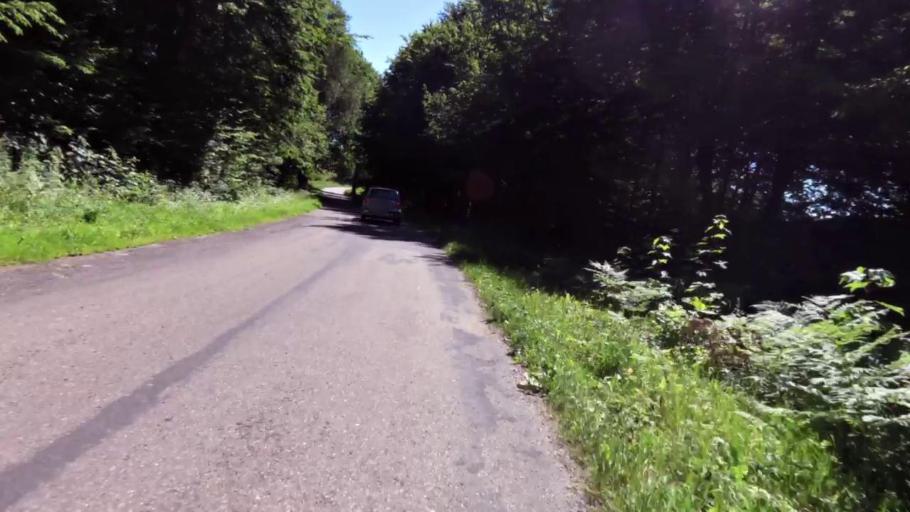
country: PL
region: West Pomeranian Voivodeship
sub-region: Powiat szczecinecki
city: Bialy Bor
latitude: 53.9672
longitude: 16.8644
